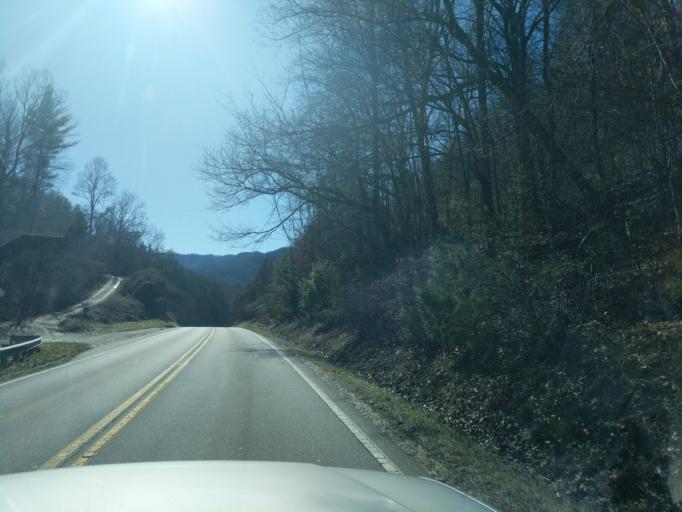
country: US
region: North Carolina
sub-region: Swain County
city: Bryson City
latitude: 35.3352
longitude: -83.5749
